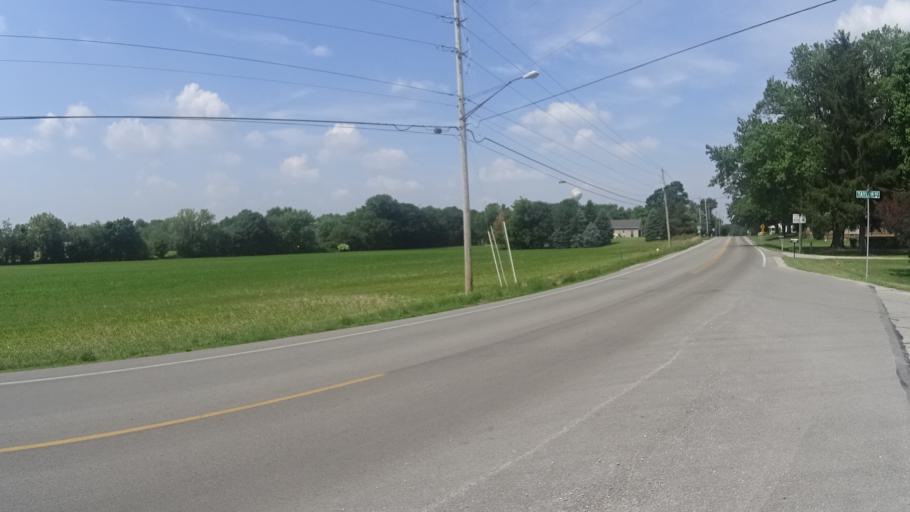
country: US
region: Ohio
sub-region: Erie County
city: Sandusky
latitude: 41.3552
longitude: -82.7247
